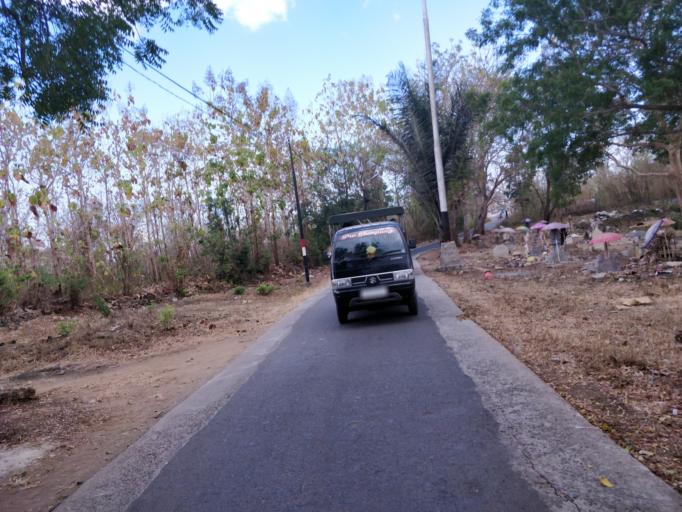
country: ID
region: Bali
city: Lembongan Kawan
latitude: -8.6843
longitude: 115.4448
